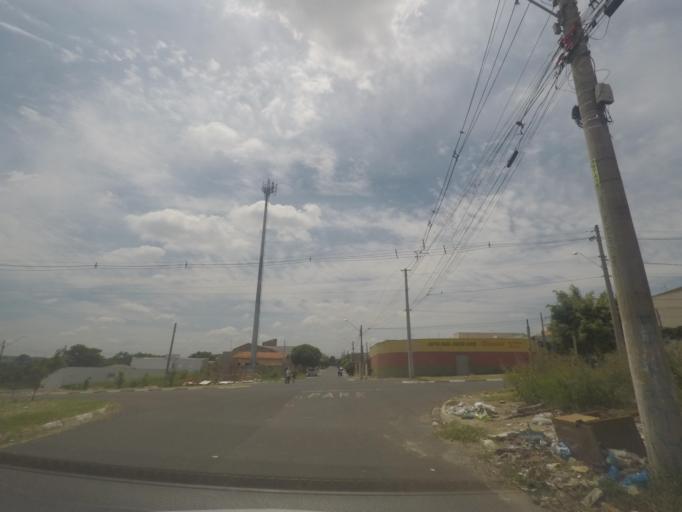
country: BR
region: Sao Paulo
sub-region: Sumare
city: Sumare
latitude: -22.7977
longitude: -47.2709
